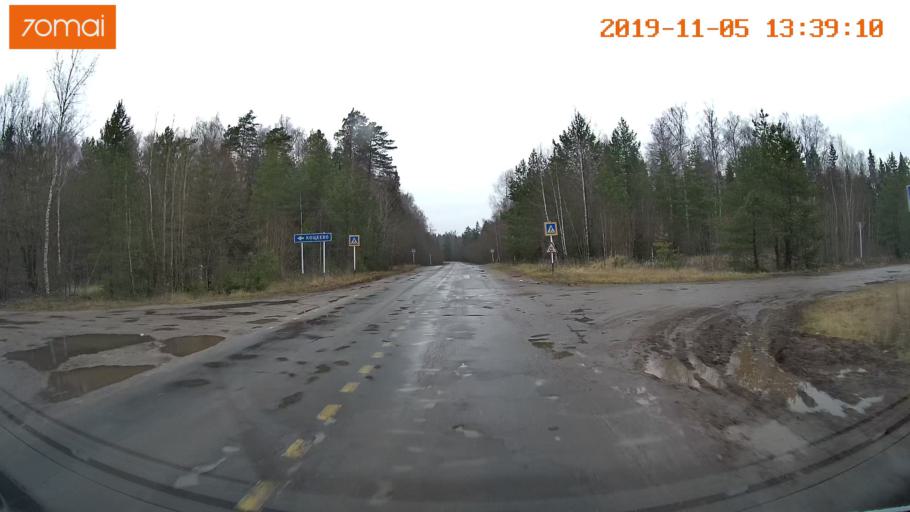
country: RU
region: Ivanovo
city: Shuya
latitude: 56.9375
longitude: 41.3869
